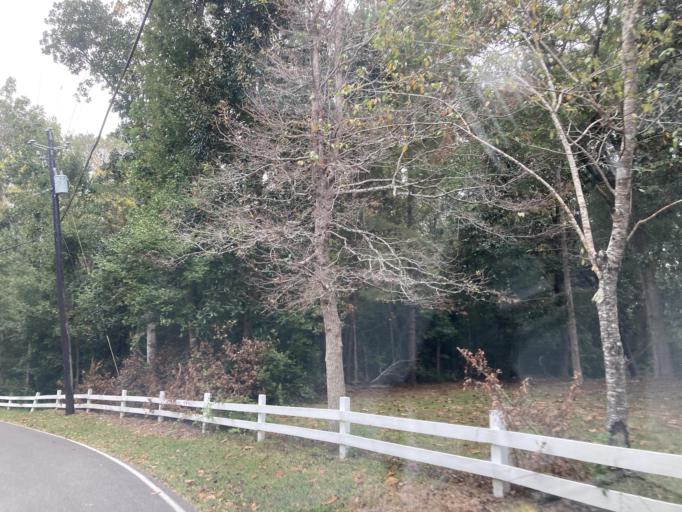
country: US
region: Mississippi
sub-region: Jackson County
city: Gulf Hills
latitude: 30.4290
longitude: -88.8350
